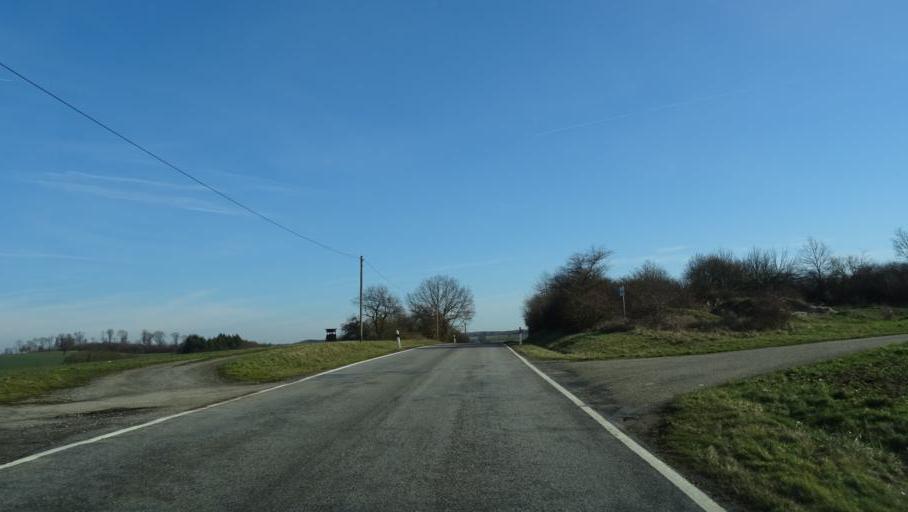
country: DE
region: Baden-Wuerttemberg
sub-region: Karlsruhe Region
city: Billigheim
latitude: 49.3725
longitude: 9.2540
